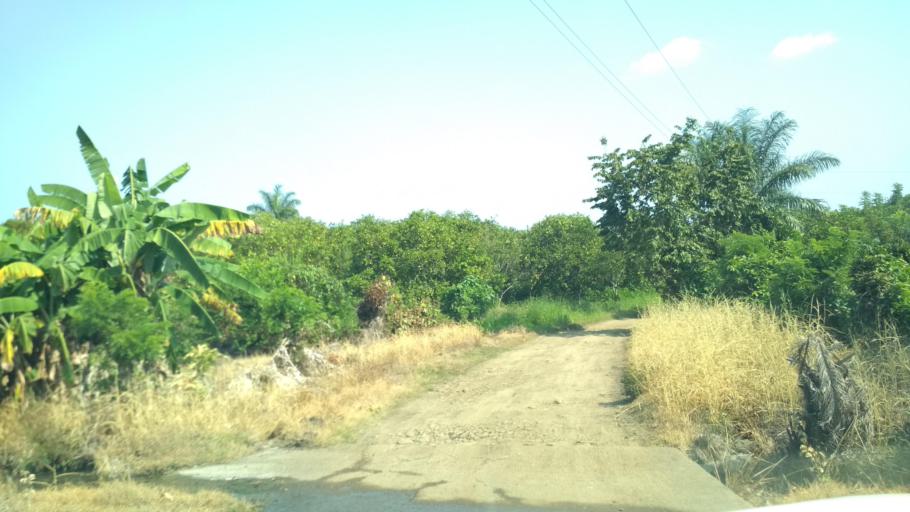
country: MX
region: Puebla
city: San Jose Acateno
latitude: 20.1721
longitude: -97.1748
